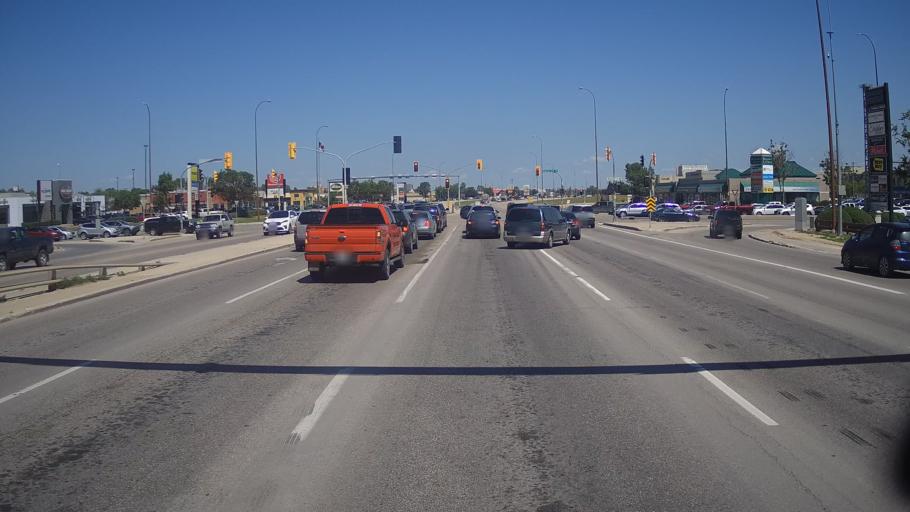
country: CA
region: Manitoba
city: Winnipeg
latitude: 49.8975
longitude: -97.0694
